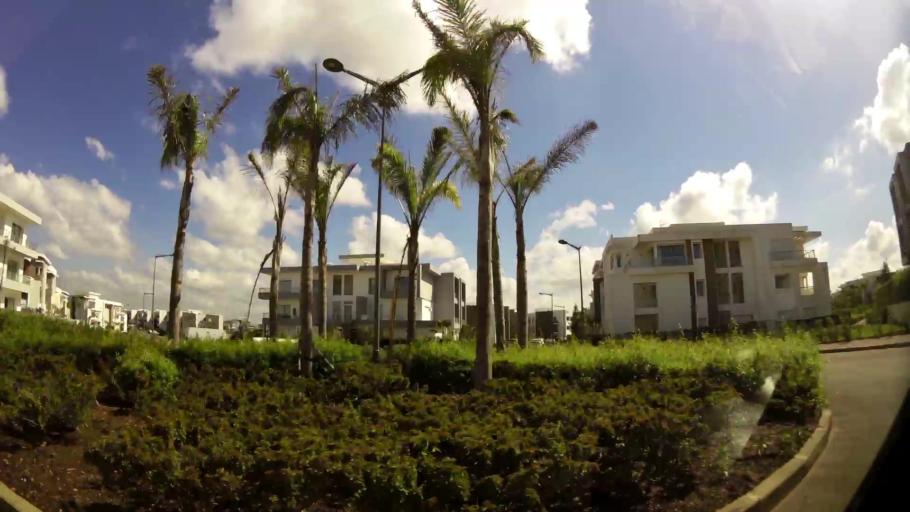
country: MA
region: Grand Casablanca
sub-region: Nouaceur
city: Bouskoura
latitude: 33.4746
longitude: -7.6048
